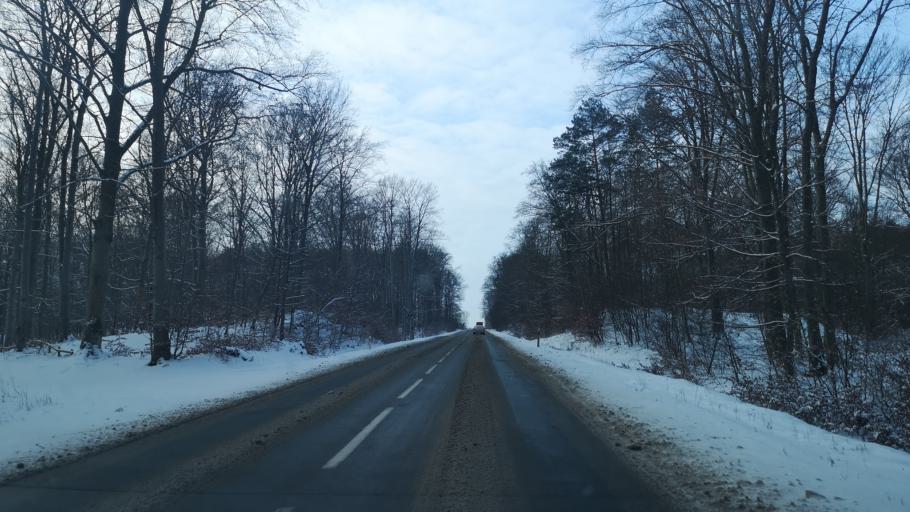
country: PL
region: Subcarpathian Voivodeship
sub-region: Powiat przeworski
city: Sieniawa
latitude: 50.2091
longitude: 22.6415
